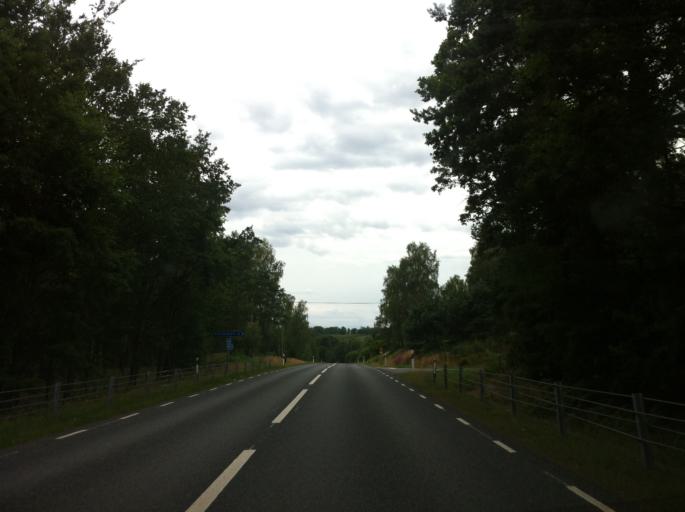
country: SE
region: Skane
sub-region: Hassleholms Kommun
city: Hastveda
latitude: 56.2096
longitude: 13.9436
